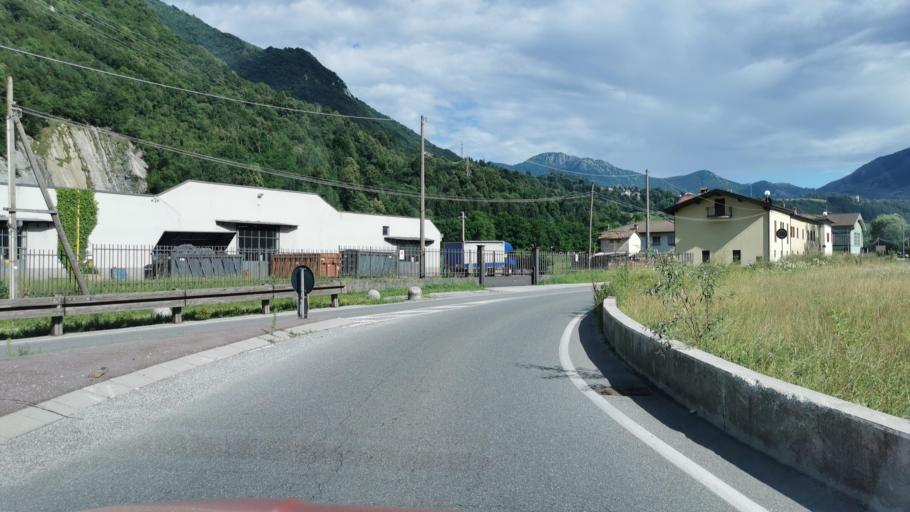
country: IT
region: Lombardy
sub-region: Provincia di Lecco
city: Pasturo
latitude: 45.9587
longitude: 9.4491
